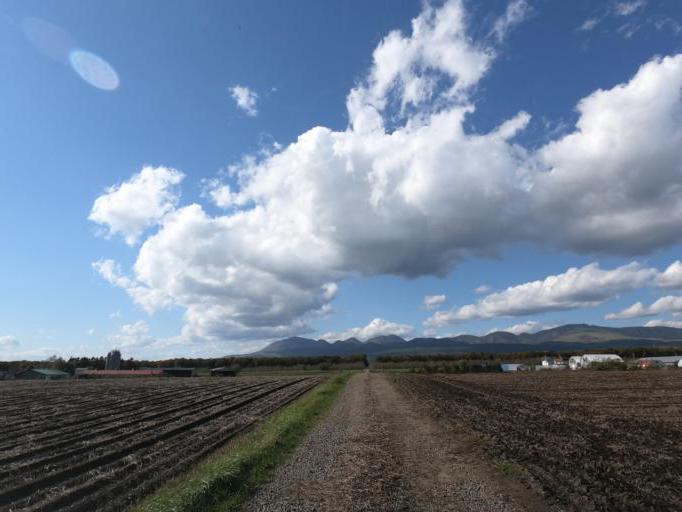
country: JP
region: Hokkaido
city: Otofuke
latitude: 43.2359
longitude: 143.2580
